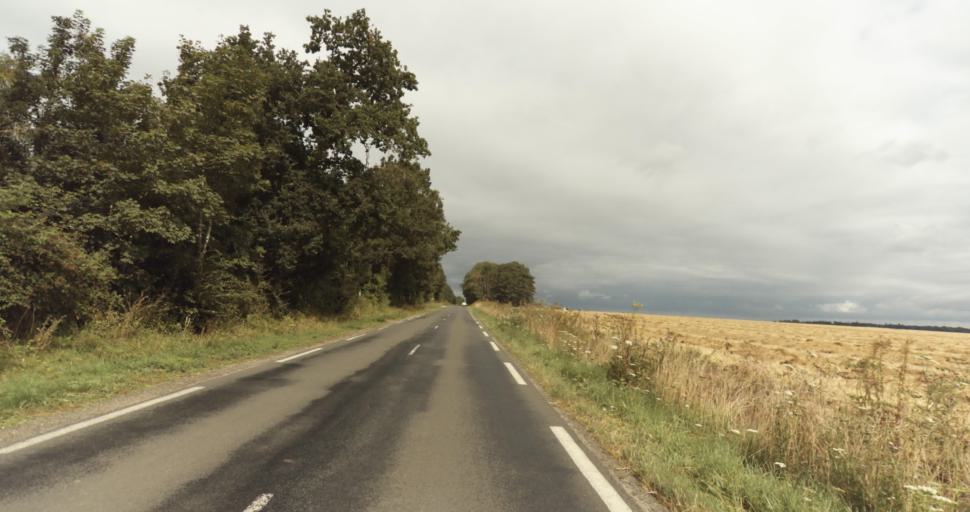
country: FR
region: Haute-Normandie
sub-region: Departement de l'Eure
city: Gravigny
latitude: 49.0164
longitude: 1.2449
